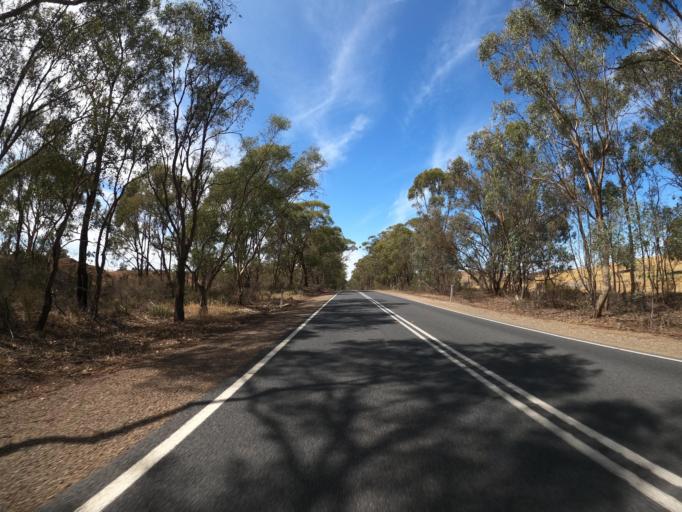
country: AU
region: Victoria
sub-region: Benalla
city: Benalla
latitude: -36.3752
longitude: 145.9745
